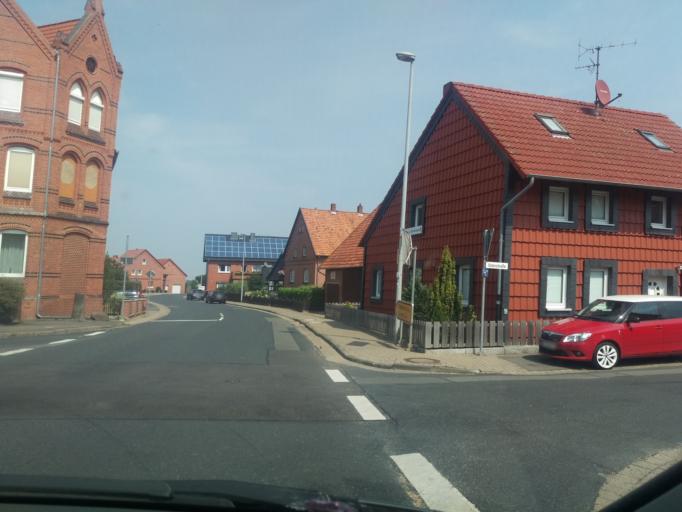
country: DE
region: Lower Saxony
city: Schellerten
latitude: 52.1525
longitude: 10.0831
